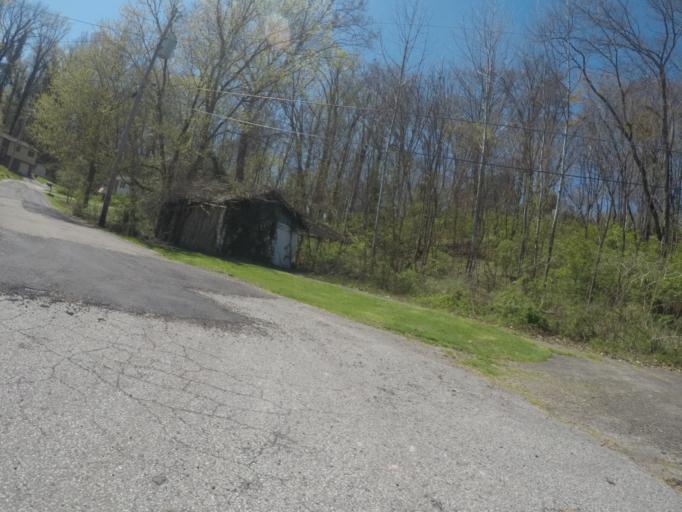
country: US
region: West Virginia
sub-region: Cabell County
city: Pea Ridge
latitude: 38.4197
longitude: -82.3205
